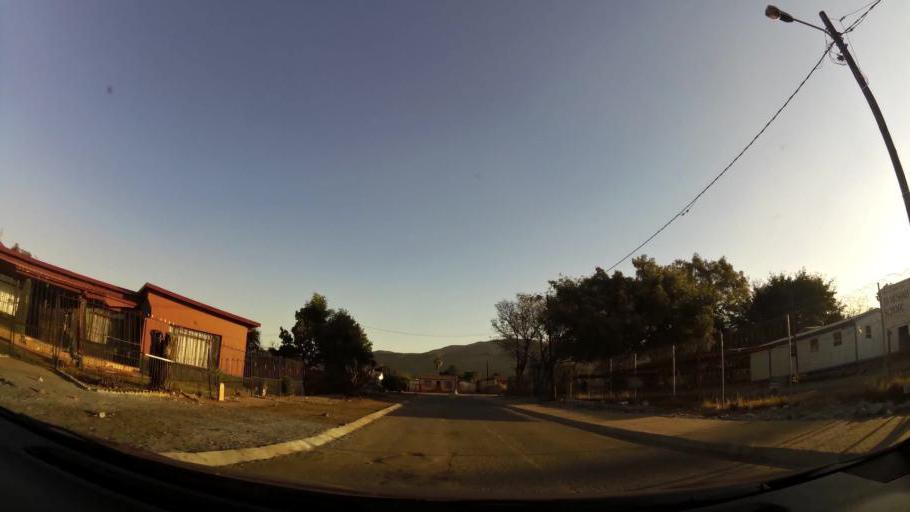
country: ZA
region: North-West
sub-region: Bojanala Platinum District Municipality
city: Rustenburg
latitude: -25.6353
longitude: 27.2080
